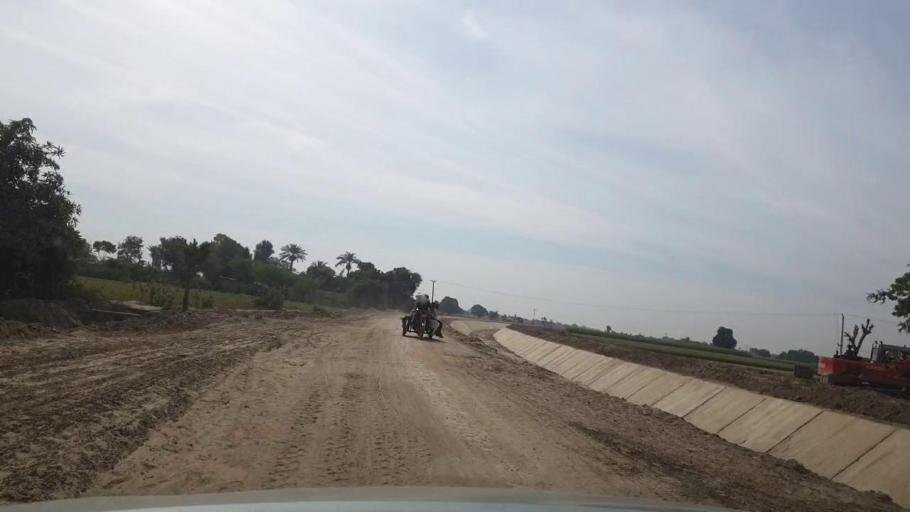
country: PK
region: Sindh
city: Kunri
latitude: 25.1601
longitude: 69.5894
